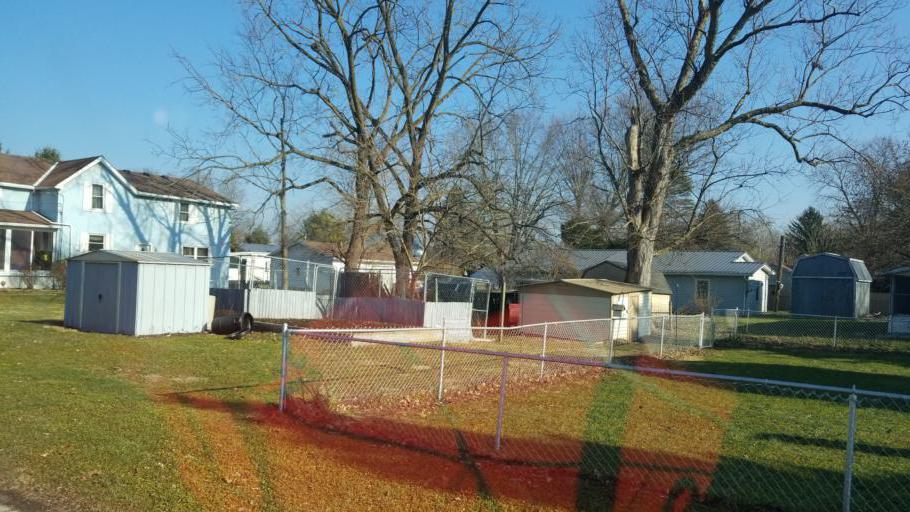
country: US
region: Ohio
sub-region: Seneca County
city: Tiffin
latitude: 41.1265
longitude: -83.1711
